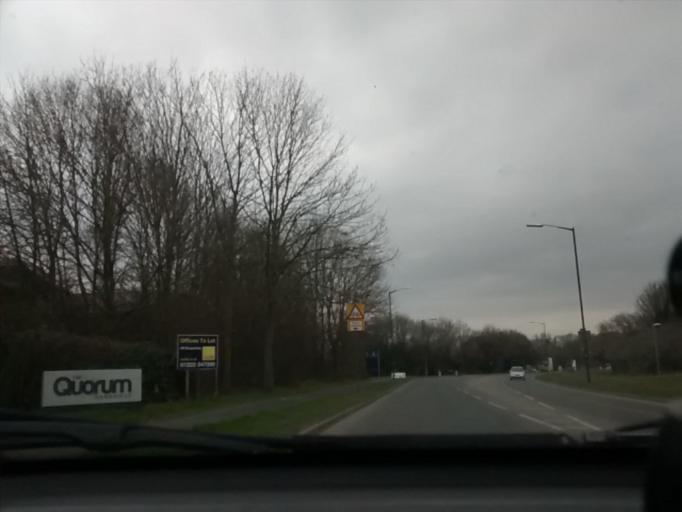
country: GB
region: England
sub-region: Cambridgeshire
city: Cambridge
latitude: 52.2069
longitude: 0.1637
